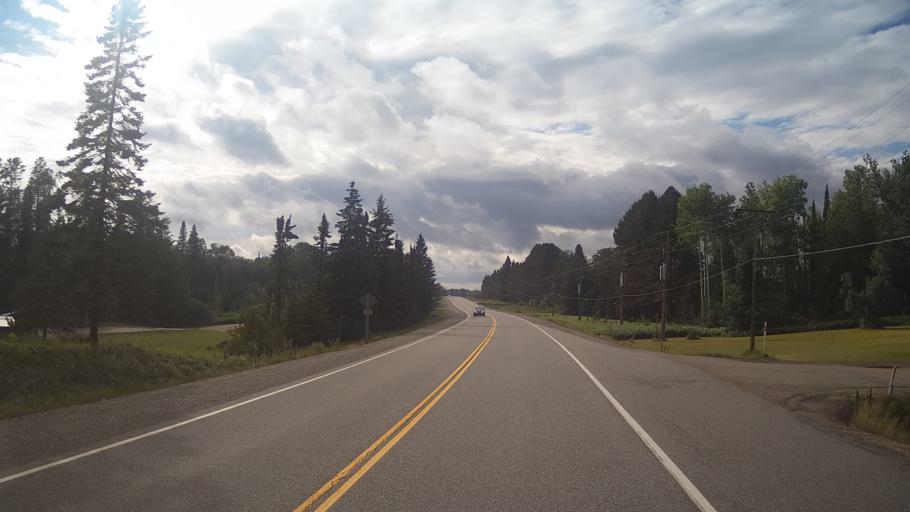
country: CA
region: Ontario
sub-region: Rainy River District
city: Atikokan
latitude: 49.0212
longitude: -90.4429
